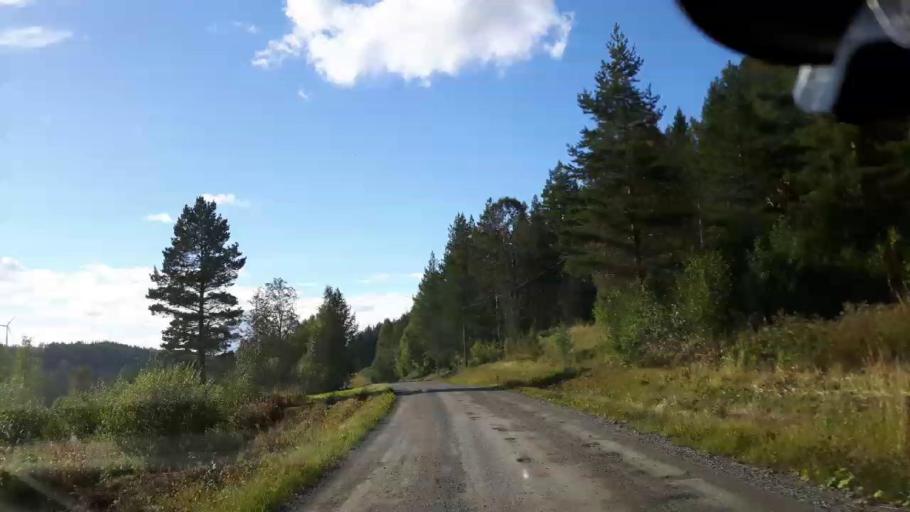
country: SE
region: Jaemtland
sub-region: Ragunda Kommun
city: Hammarstrand
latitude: 63.4754
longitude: 16.1653
